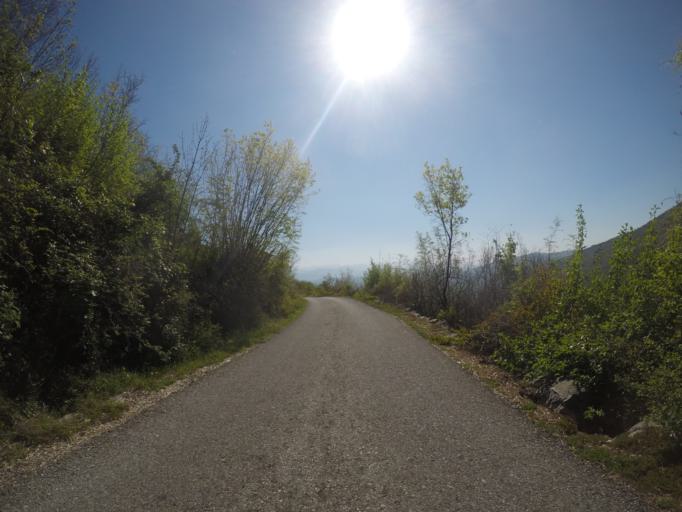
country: ME
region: Danilovgrad
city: Danilovgrad
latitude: 42.5162
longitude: 19.0643
